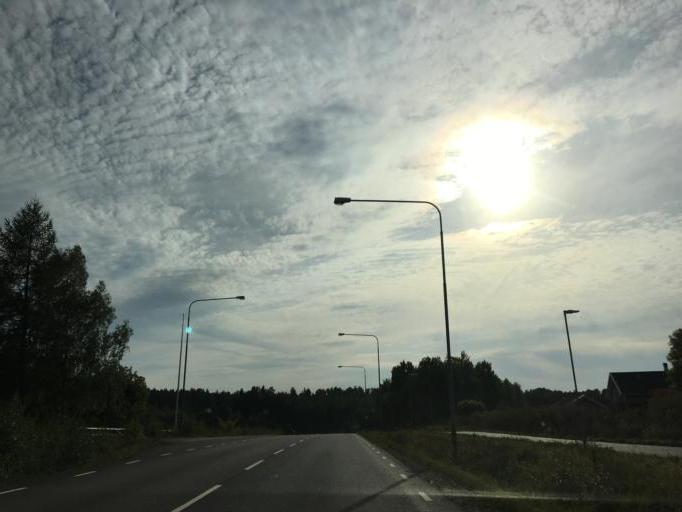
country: SE
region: Soedermanland
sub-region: Eskilstuna Kommun
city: Torshalla
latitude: 59.4315
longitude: 16.4559
